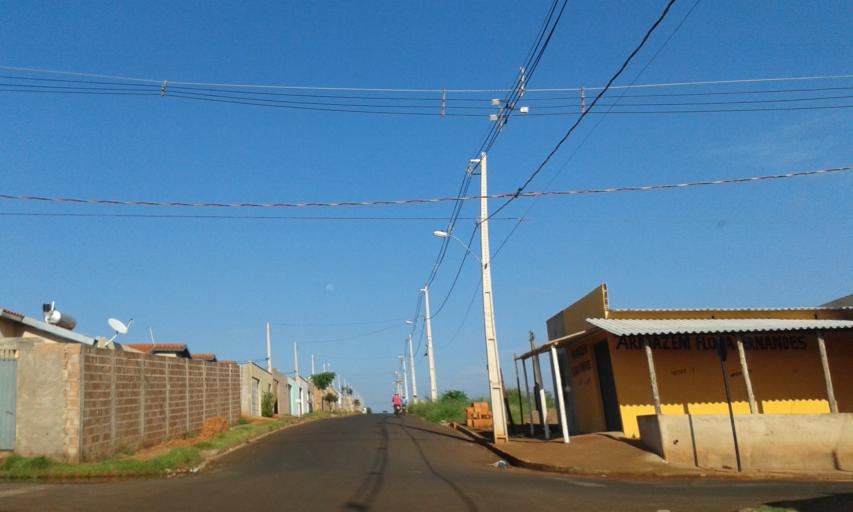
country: BR
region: Minas Gerais
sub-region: Ituiutaba
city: Ituiutaba
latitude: -19.0154
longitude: -49.4552
